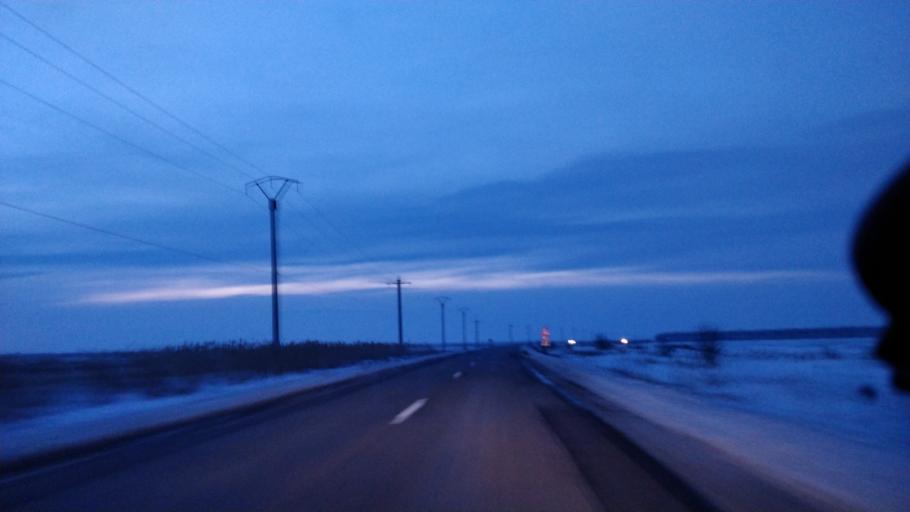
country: RO
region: Vrancea
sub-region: Comuna Vulturu
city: Vadu Rosca
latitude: 45.5946
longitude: 27.4713
